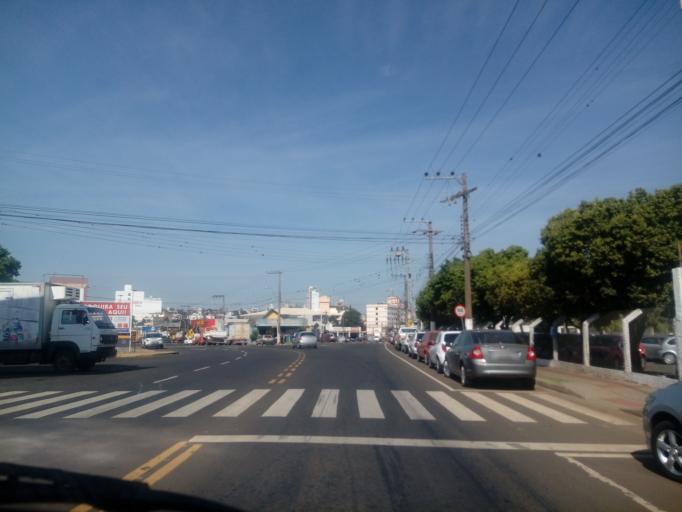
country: BR
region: Santa Catarina
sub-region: Chapeco
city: Chapeco
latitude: -27.0918
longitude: -52.6229
